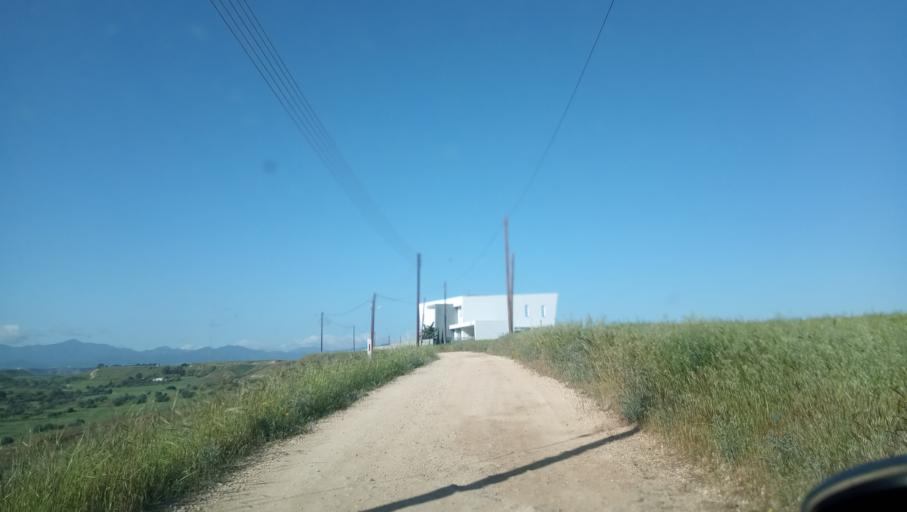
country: CY
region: Lefkosia
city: Tseri
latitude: 35.0685
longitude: 33.3140
